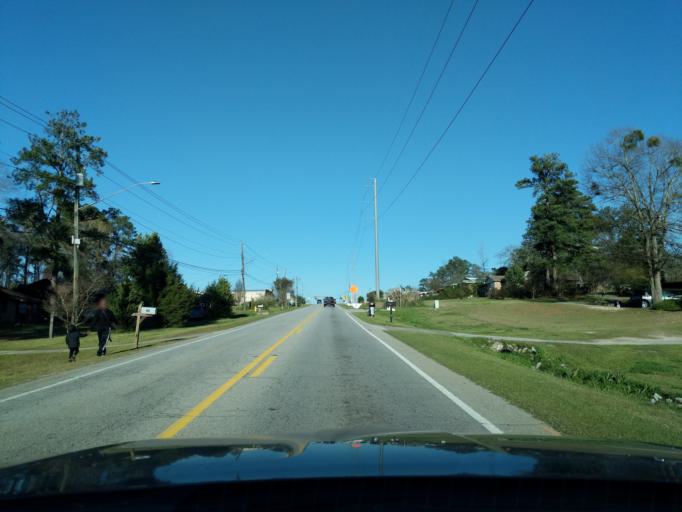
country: US
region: Georgia
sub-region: Columbia County
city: Grovetown
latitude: 33.4527
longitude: -82.2108
